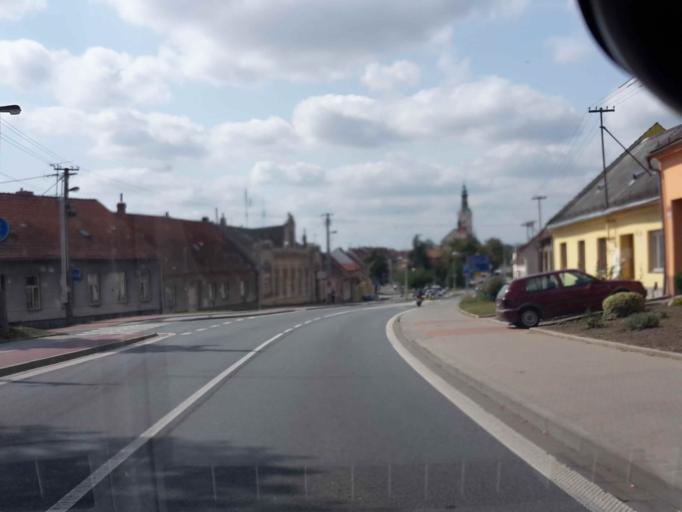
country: CZ
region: South Moravian
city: Rousinov
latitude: 49.2052
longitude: 16.8860
